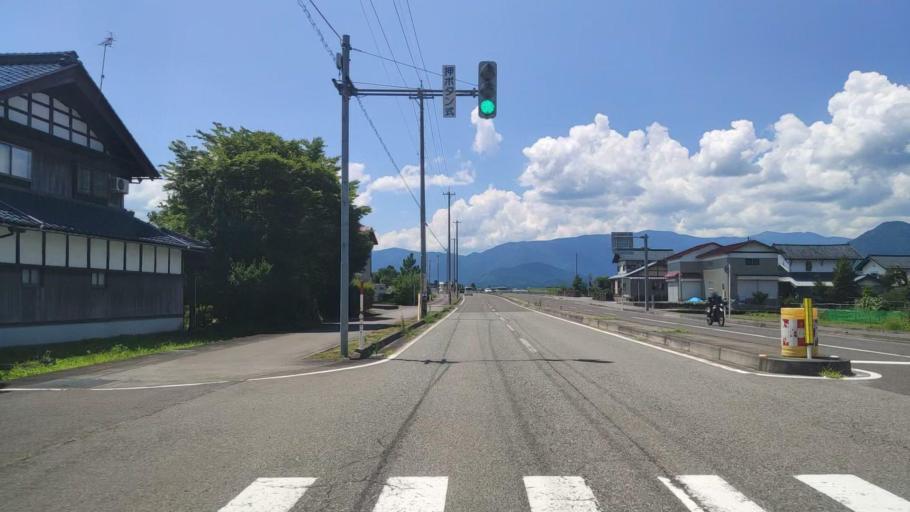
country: JP
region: Fukui
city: Ono
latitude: 36.0022
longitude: 136.5090
